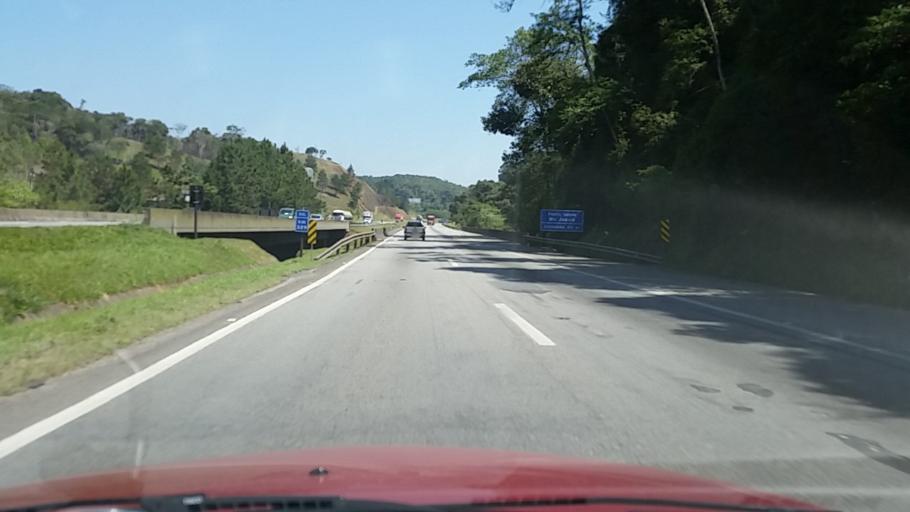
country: BR
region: Sao Paulo
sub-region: Juquitiba
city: Juquitiba
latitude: -23.9400
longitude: -47.0895
